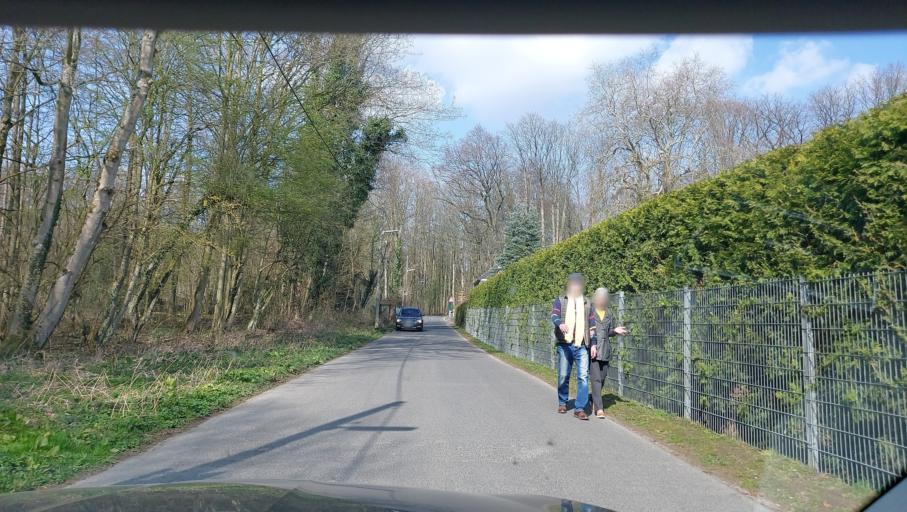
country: DE
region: North Rhine-Westphalia
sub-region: Regierungsbezirk Dusseldorf
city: Erkrath
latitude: 51.2439
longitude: 6.8648
